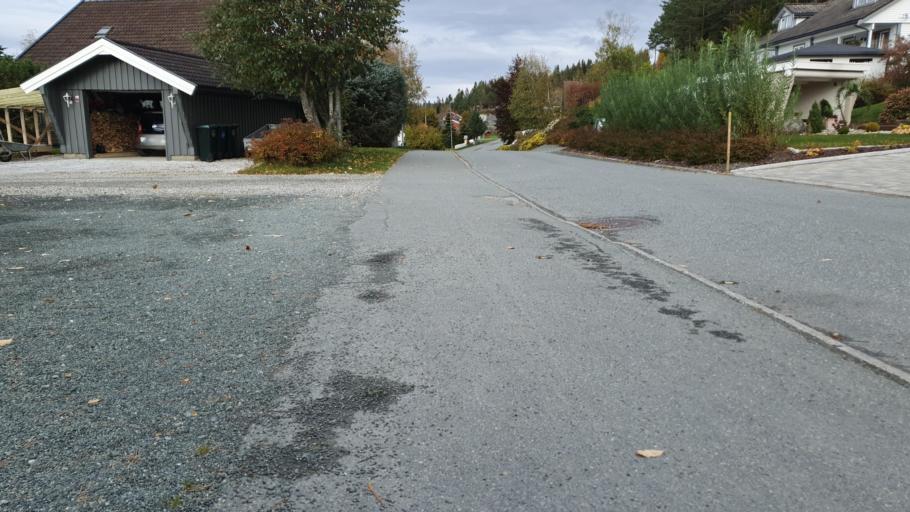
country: NO
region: Sor-Trondelag
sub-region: Klaebu
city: Klaebu
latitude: 63.2978
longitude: 10.4654
